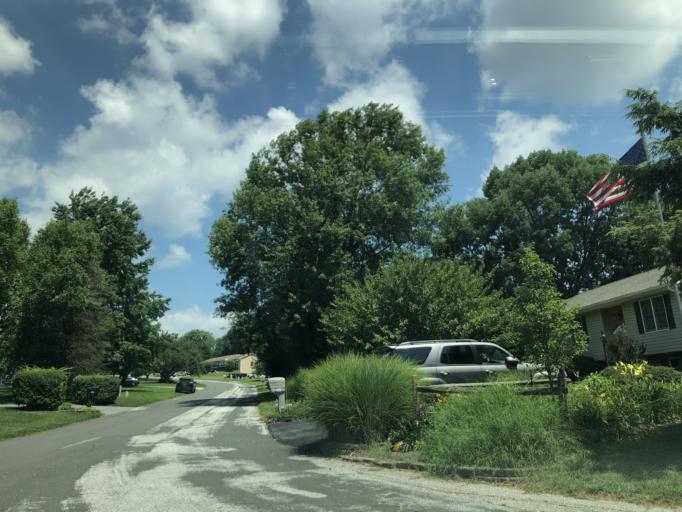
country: US
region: Maryland
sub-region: Carroll County
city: Westminster
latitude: 39.5295
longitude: -76.9366
